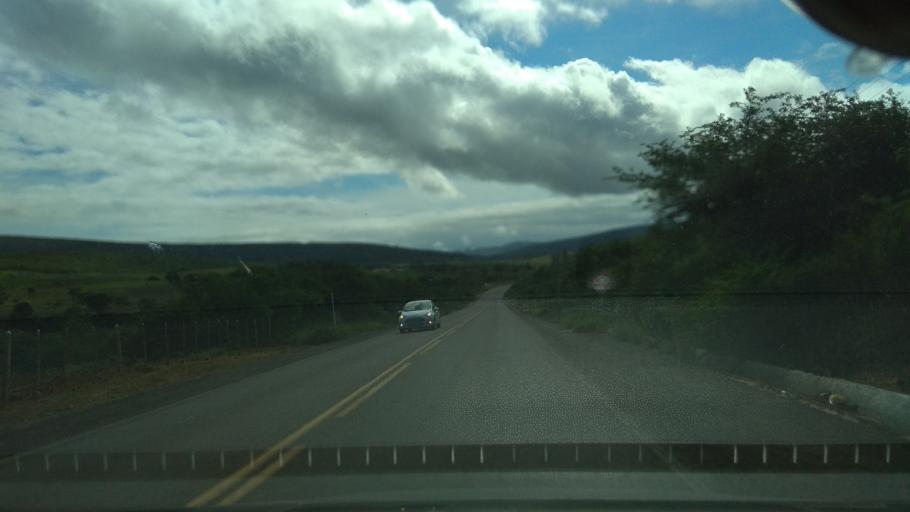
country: BR
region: Bahia
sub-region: Jaguaquara
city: Jaguaquara
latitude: -13.4297
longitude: -39.9252
